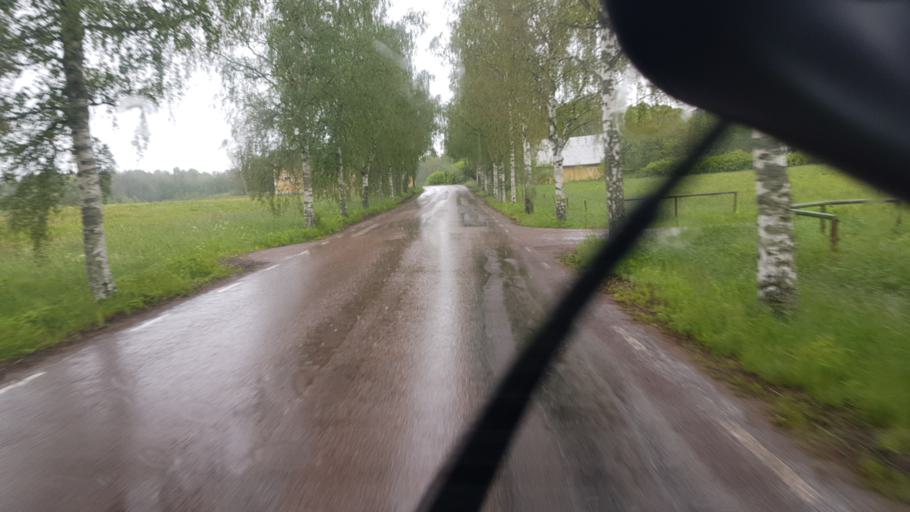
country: SE
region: Vaermland
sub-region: Arvika Kommun
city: Arvika
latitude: 59.7123
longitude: 12.5051
